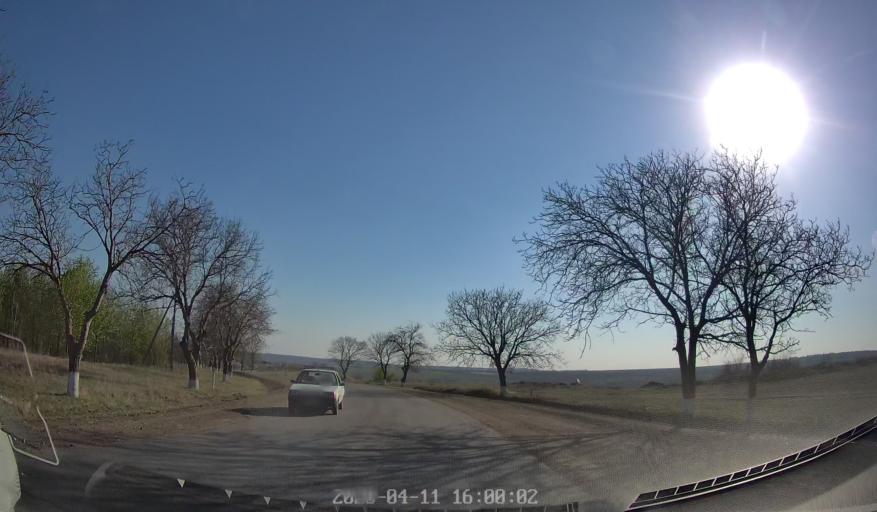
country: MD
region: Chisinau
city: Vadul lui Voda
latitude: 47.0783
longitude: 29.1363
